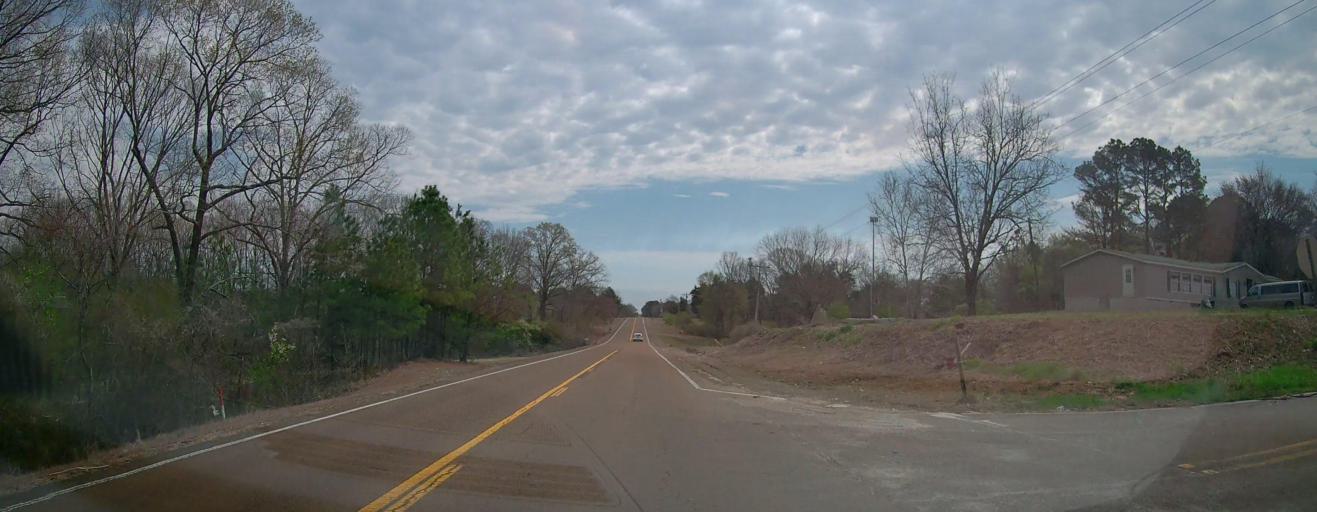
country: US
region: Mississippi
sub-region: Marshall County
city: Holly Springs
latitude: 34.8227
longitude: -89.5488
